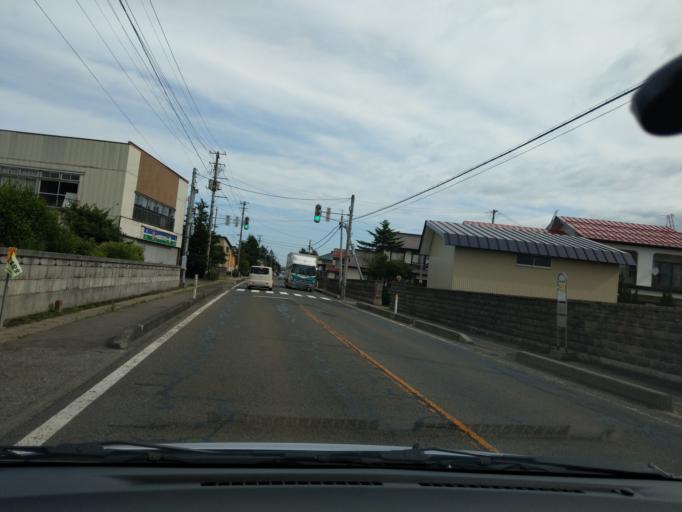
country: JP
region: Akita
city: Yokotemachi
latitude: 39.3955
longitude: 140.5653
